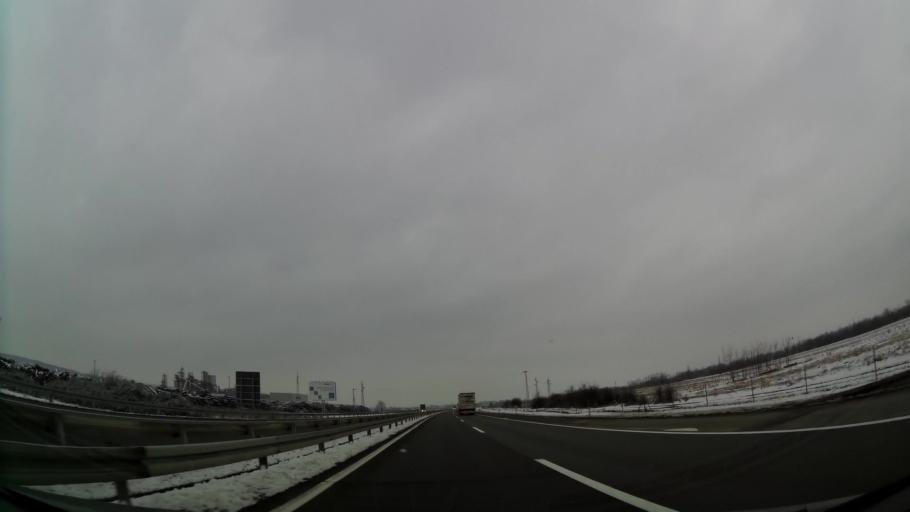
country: RS
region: Central Serbia
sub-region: Sumadijski Okrug
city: Lapovo
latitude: 44.1648
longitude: 21.1070
